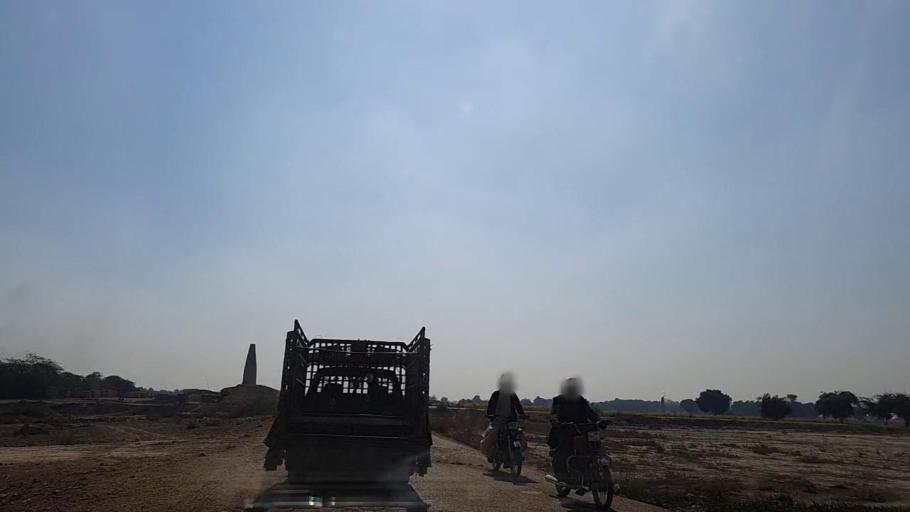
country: PK
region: Sindh
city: Sakrand
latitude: 26.2918
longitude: 68.1080
